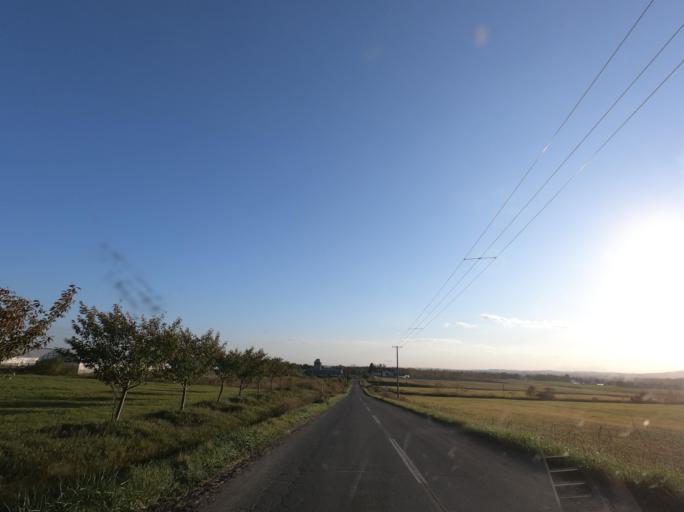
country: JP
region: Hokkaido
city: Iwamizawa
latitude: 42.9994
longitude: 141.8756
